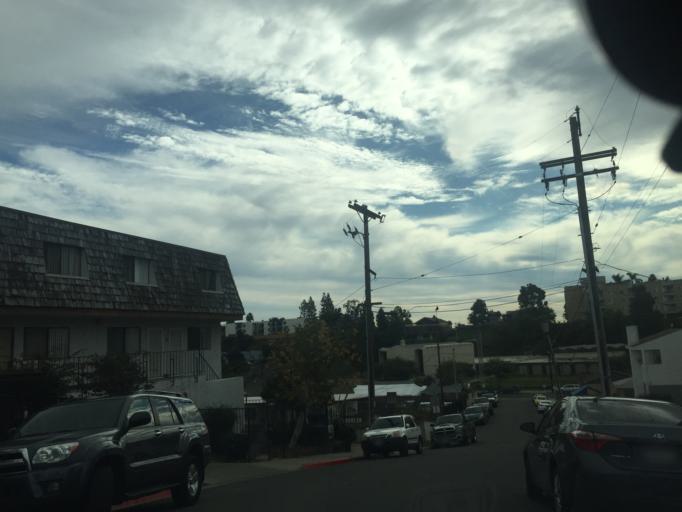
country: US
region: California
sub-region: San Diego County
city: Lemon Grove
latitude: 32.7560
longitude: -117.0815
